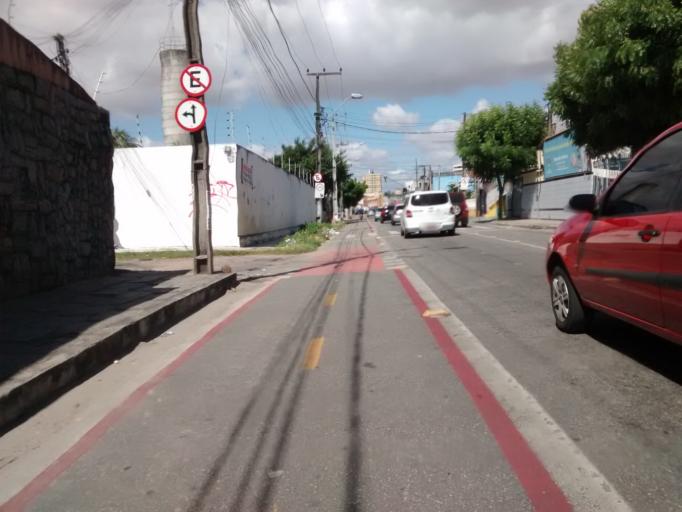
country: BR
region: Ceara
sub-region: Fortaleza
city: Fortaleza
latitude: -3.7237
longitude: -38.5507
